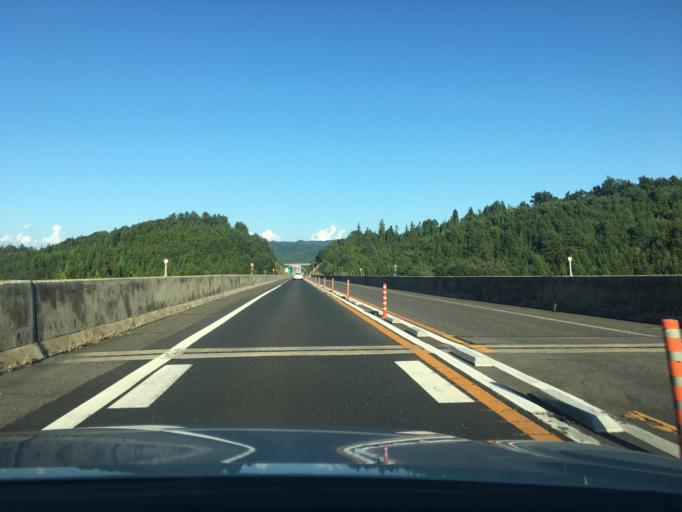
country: JP
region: Fukushima
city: Kitakata
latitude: 37.5651
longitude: 139.6179
